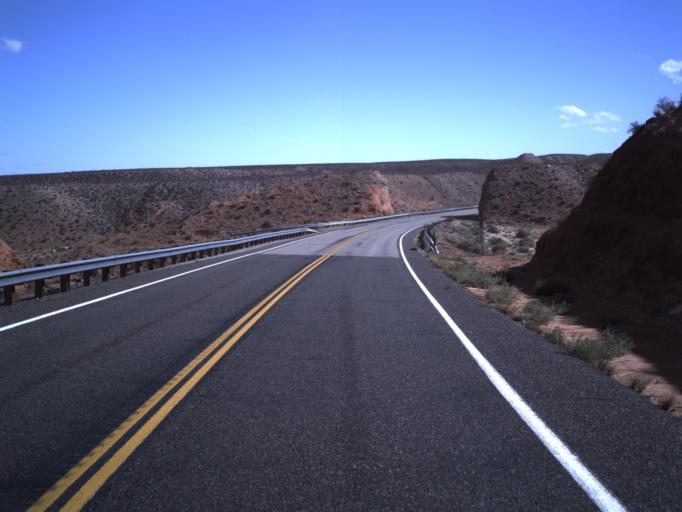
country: US
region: Utah
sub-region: Wayne County
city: Loa
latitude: 38.1426
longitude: -110.6108
